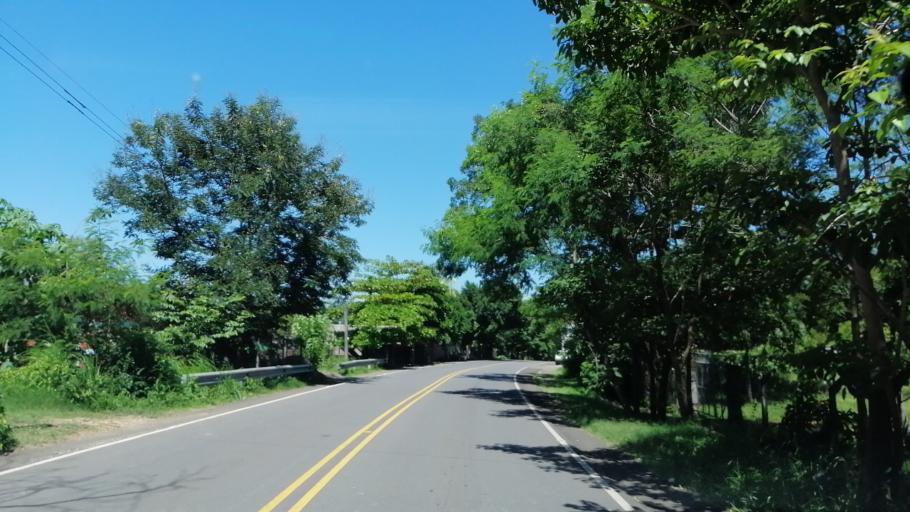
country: SV
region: Morazan
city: Cacaopera
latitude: 13.8101
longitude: -88.1624
